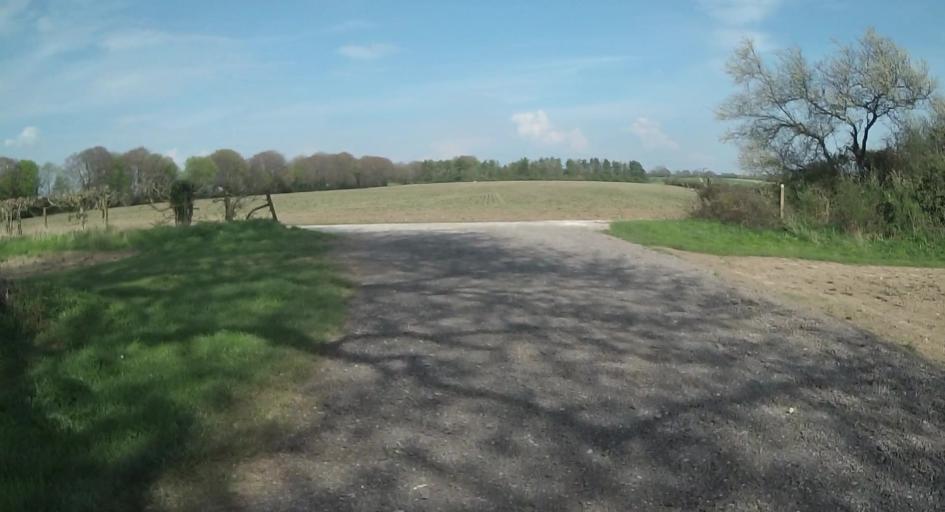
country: GB
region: England
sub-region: Hampshire
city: Basingstoke
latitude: 51.2043
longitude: -1.1557
